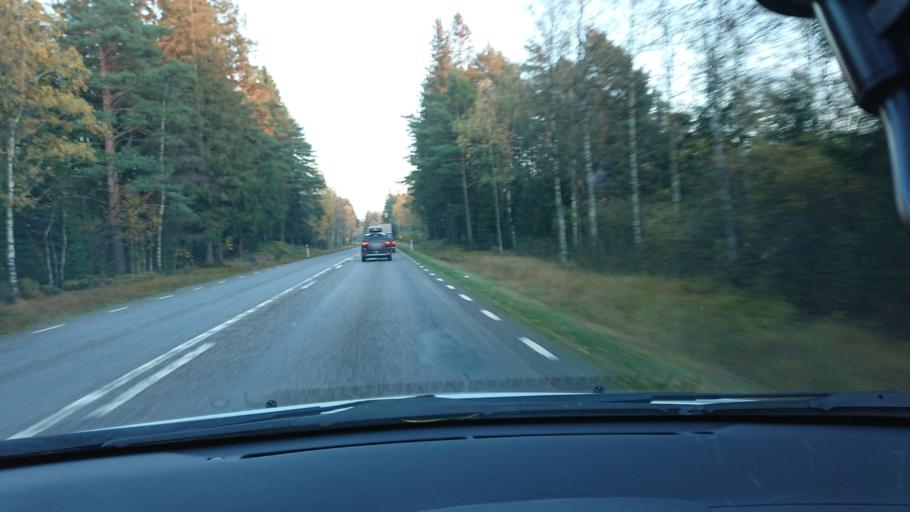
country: SE
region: Halland
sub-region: Laholms Kommun
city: Veinge
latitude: 56.7178
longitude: 13.1845
